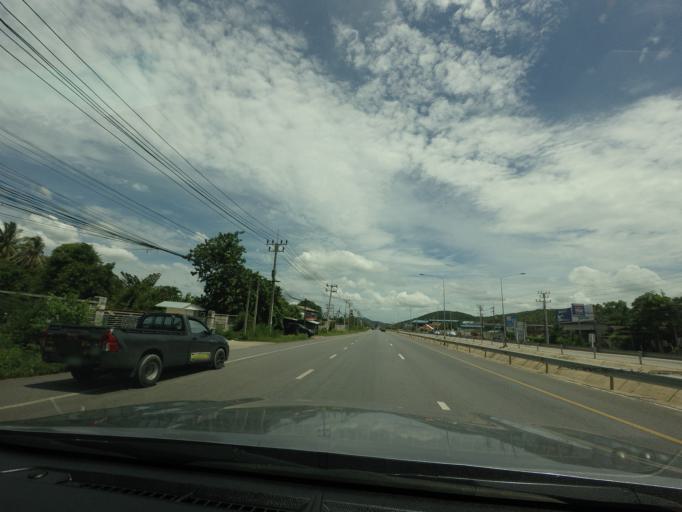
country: TH
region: Songkhla
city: Ban Mai
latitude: 7.2072
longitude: 100.5559
